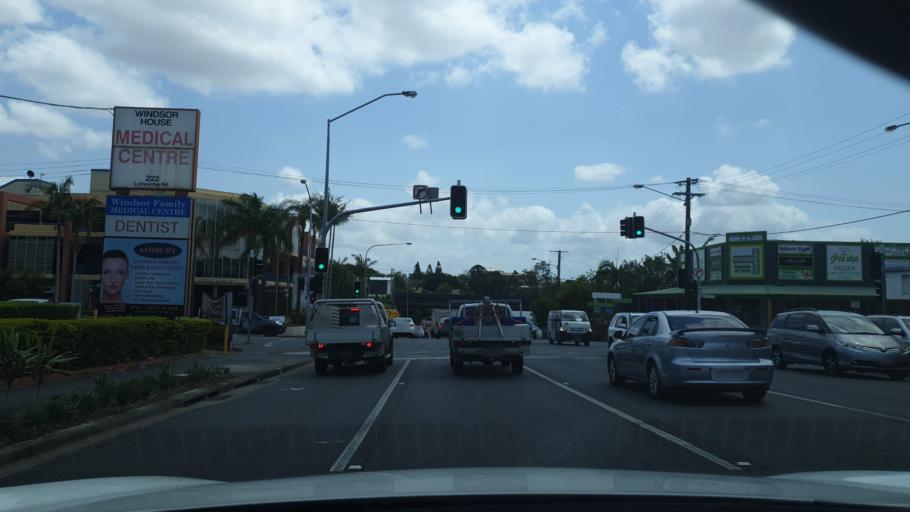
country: AU
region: Queensland
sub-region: Brisbane
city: Windsor
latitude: -27.4357
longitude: 153.0314
